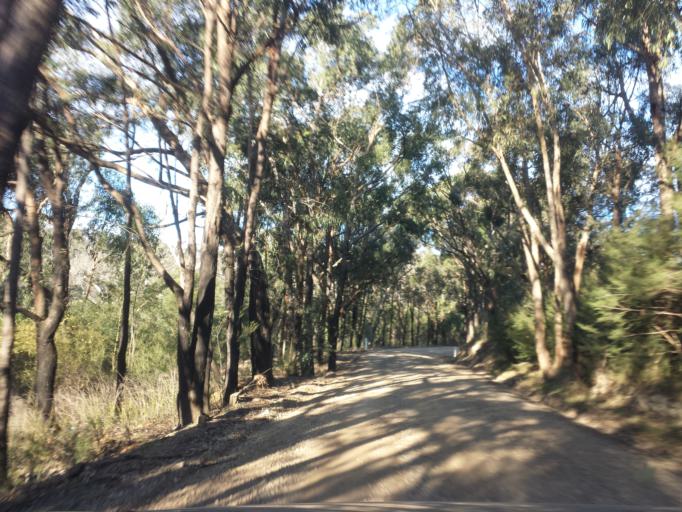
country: AU
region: Victoria
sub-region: Yarra Ranges
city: Yarra Glen
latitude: -37.5814
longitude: 145.3994
